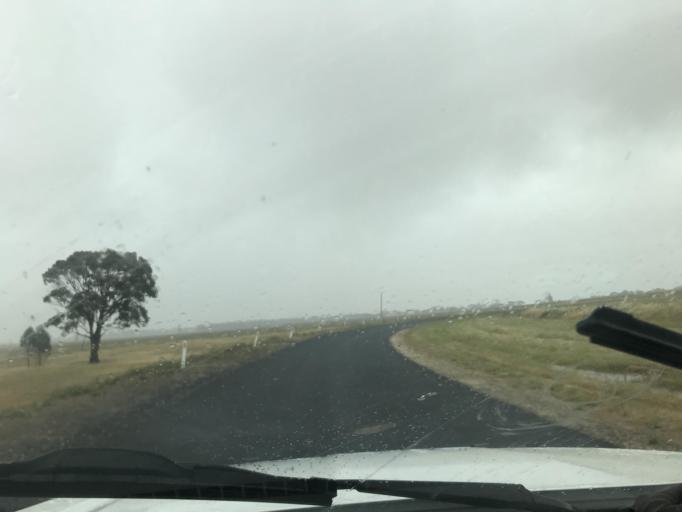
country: AU
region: South Australia
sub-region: Tatiara
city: Bordertown
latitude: -36.3128
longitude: 141.1449
